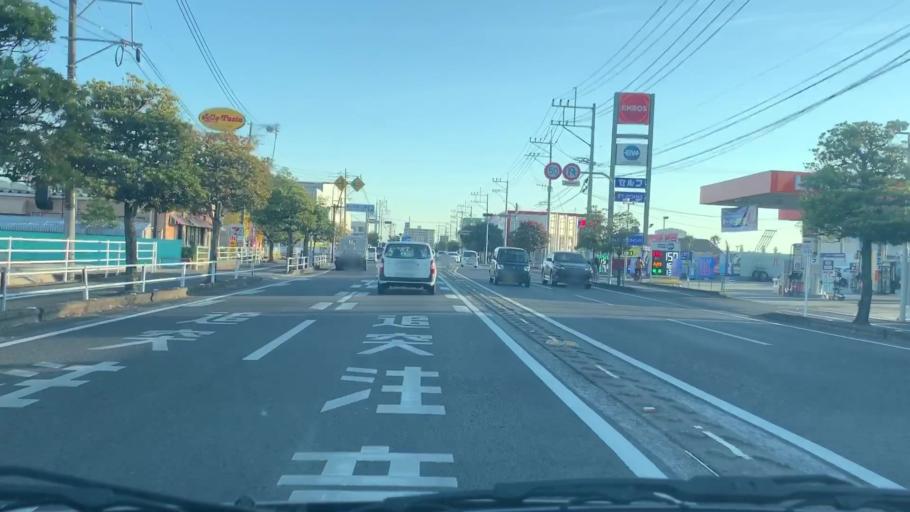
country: JP
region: Saga Prefecture
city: Saga-shi
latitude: 33.2651
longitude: 130.2720
